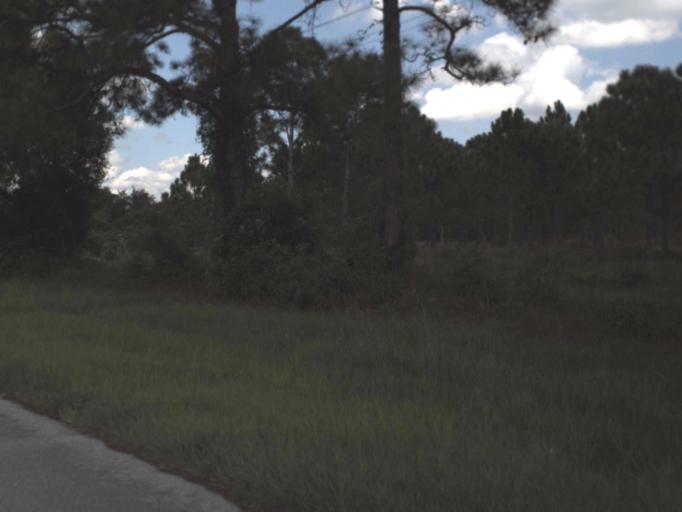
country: US
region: Florida
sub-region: Okeechobee County
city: Okeechobee
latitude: 27.3655
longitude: -81.0655
